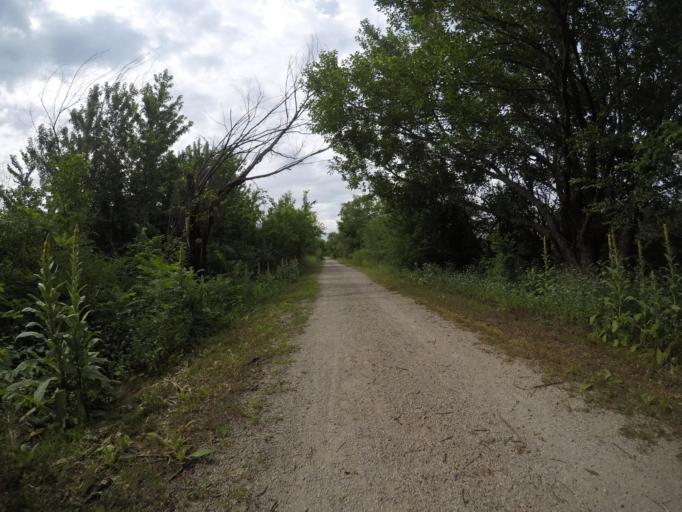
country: US
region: Kansas
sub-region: Anderson County
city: Garnett
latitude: 38.4176
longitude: -95.2627
